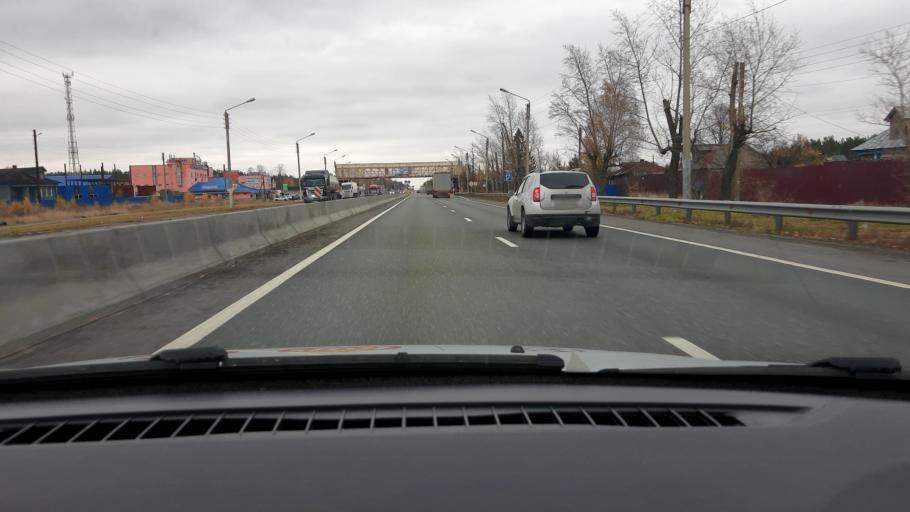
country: RU
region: Nizjnij Novgorod
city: Pyra
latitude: 56.2933
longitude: 43.3490
